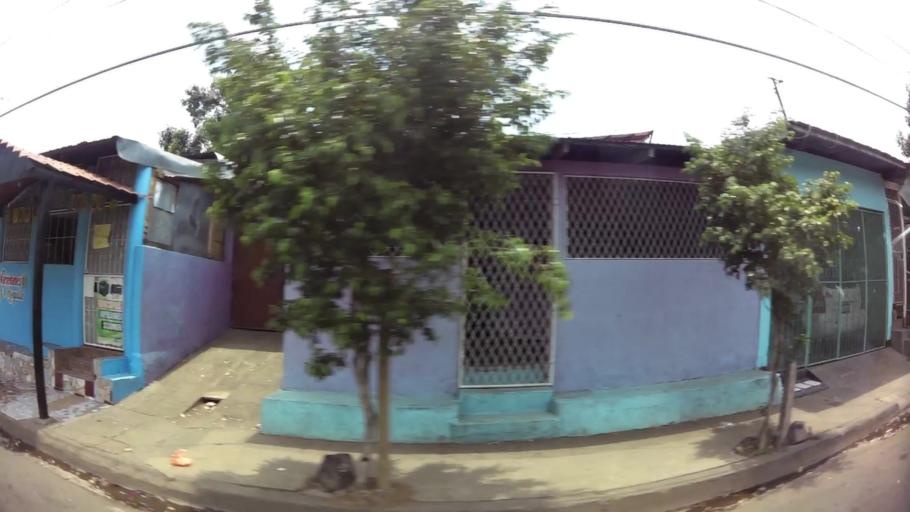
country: NI
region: Managua
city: Managua
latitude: 12.1150
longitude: -86.2977
